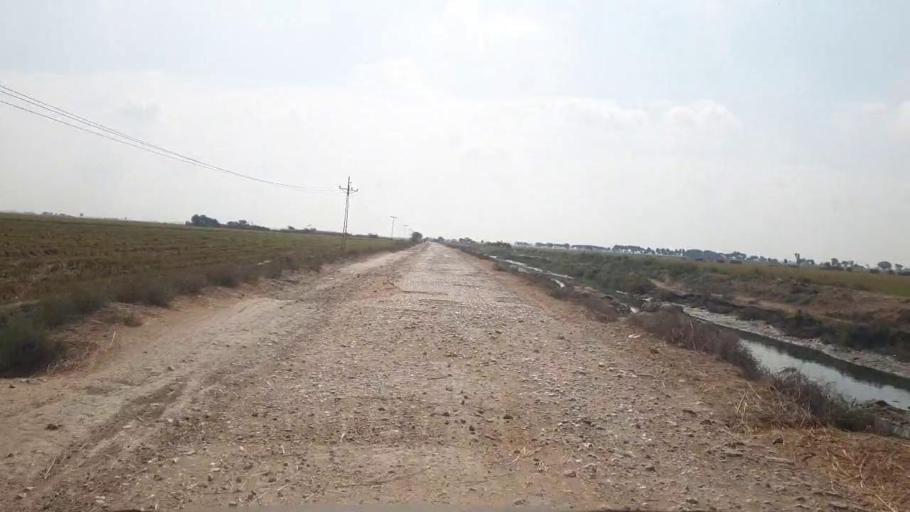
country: PK
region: Sindh
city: Kario
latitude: 24.6317
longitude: 68.5504
